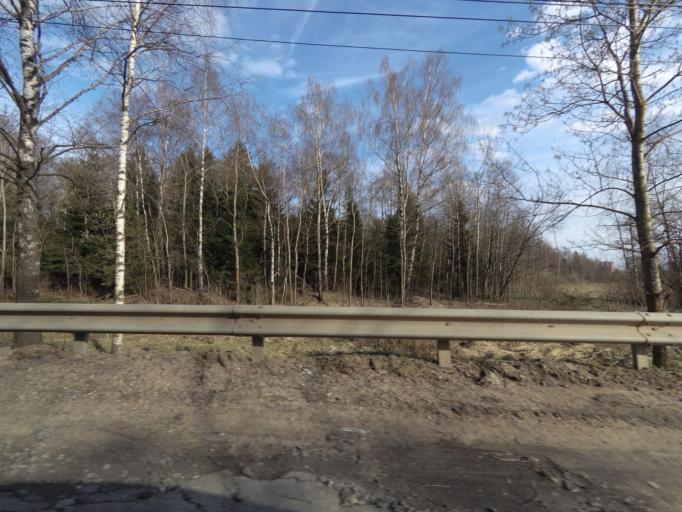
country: RU
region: Moskovskaya
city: Lugovaya
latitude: 56.0305
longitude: 37.4653
